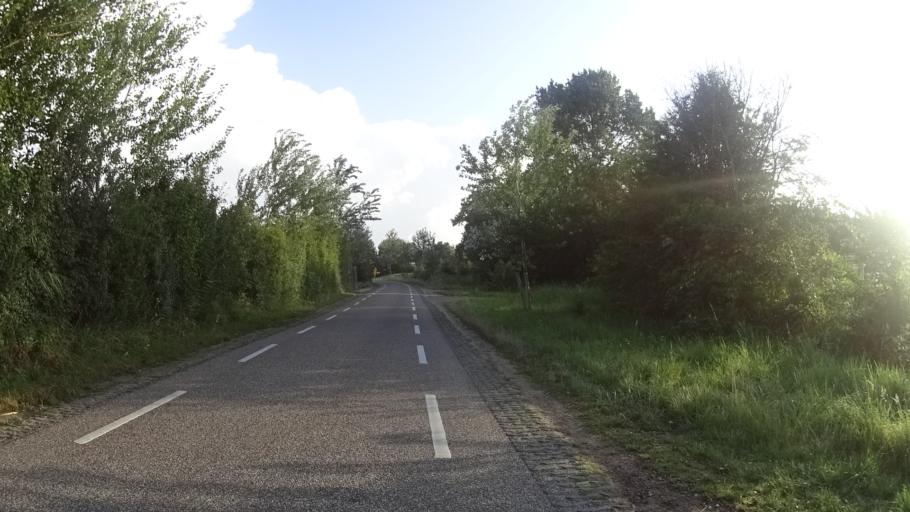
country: NL
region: Zeeland
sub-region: Gemeente Veere
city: Veere
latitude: 51.5406
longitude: 3.6266
